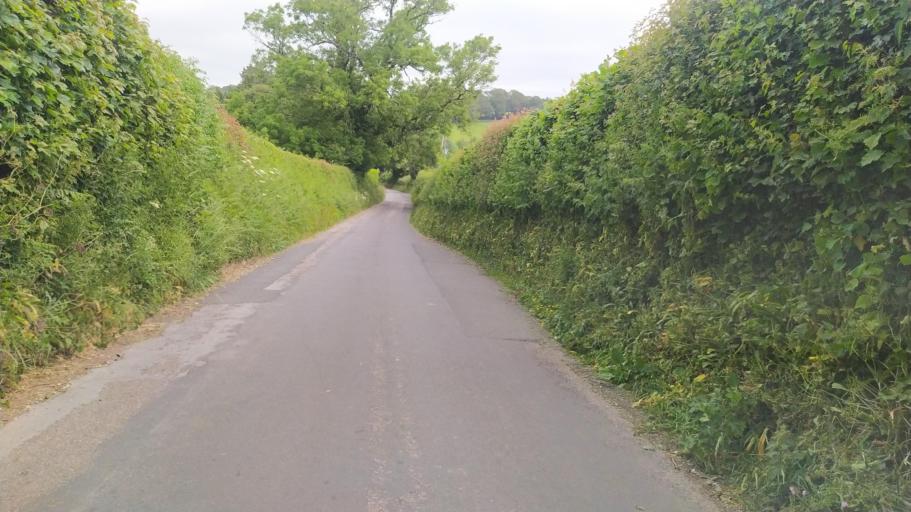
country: GB
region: England
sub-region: Somerset
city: Yeovil
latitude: 50.8365
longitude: -2.6056
